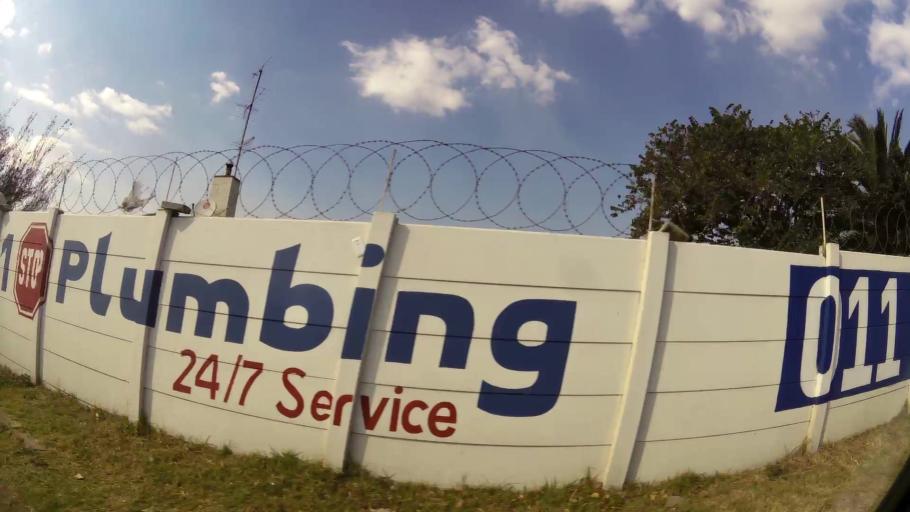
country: ZA
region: Gauteng
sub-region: Ekurhuleni Metropolitan Municipality
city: Germiston
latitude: -26.1840
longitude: 28.1727
